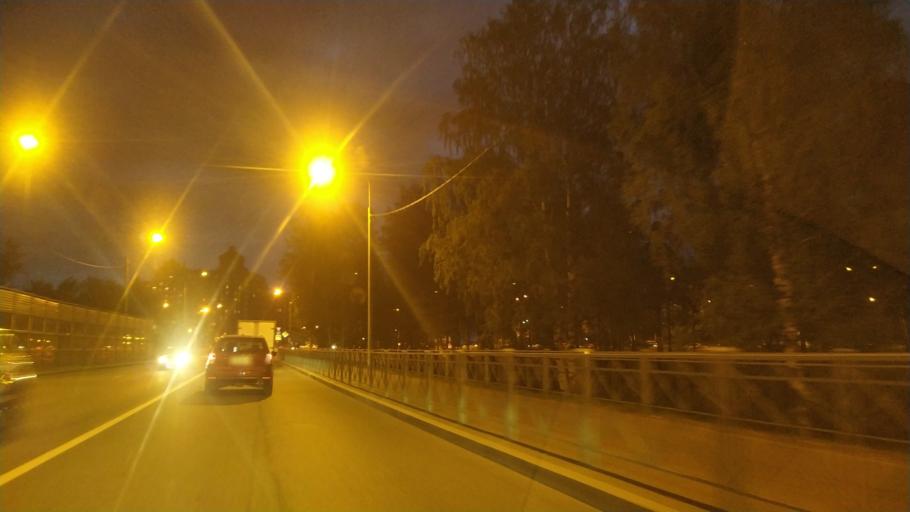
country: RU
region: St.-Petersburg
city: Ozerki
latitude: 60.0290
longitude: 30.3175
